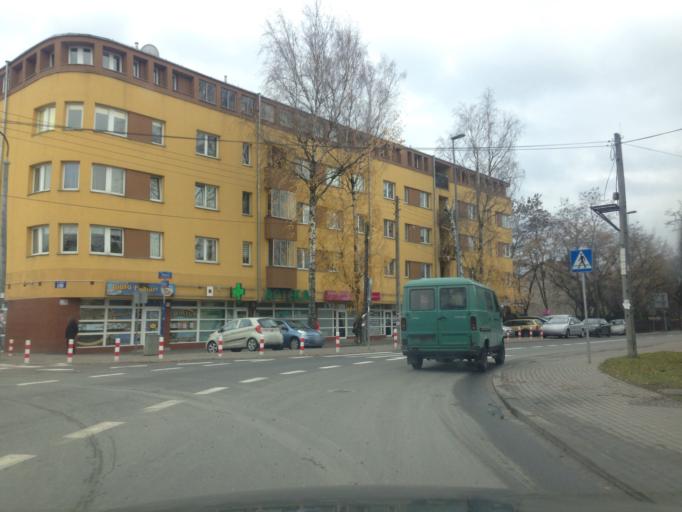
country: PL
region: Masovian Voivodeship
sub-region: Warszawa
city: Rembertow
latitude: 52.2561
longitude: 21.1565
